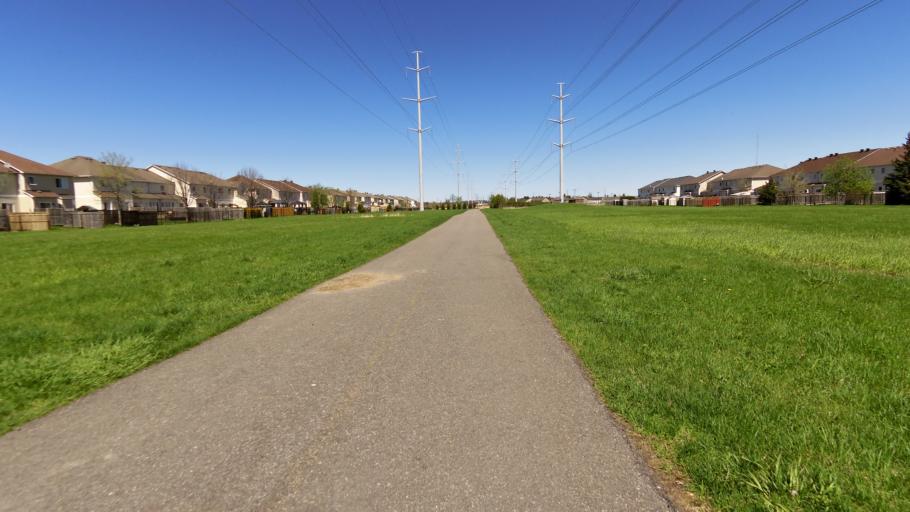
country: CA
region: Ontario
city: Clarence-Rockland
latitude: 45.4729
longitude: -75.4642
